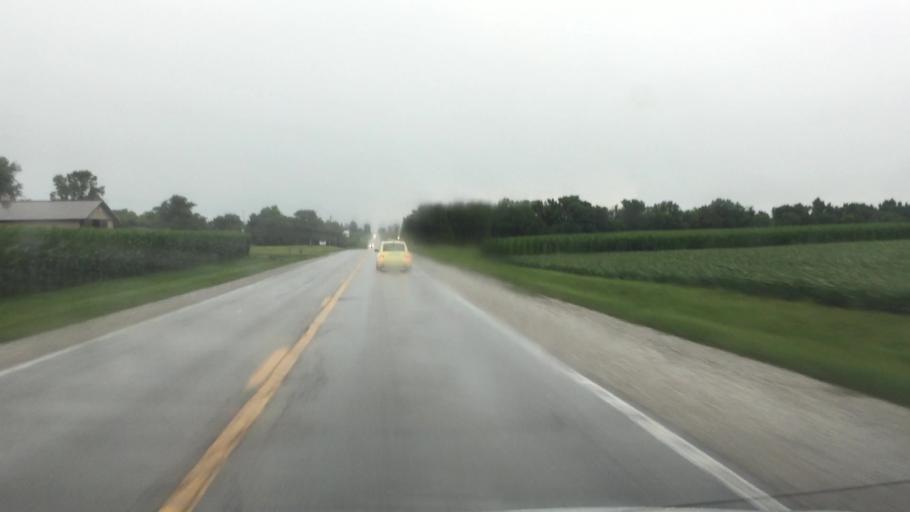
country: US
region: Illinois
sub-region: Hancock County
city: Carthage
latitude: 40.4546
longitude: -91.1397
